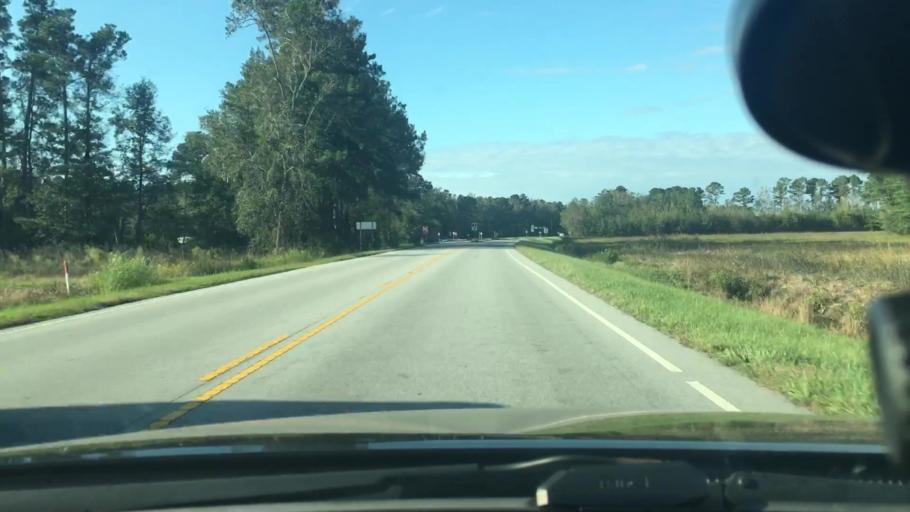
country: US
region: North Carolina
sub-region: Craven County
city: Vanceboro
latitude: 35.3306
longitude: -77.1497
